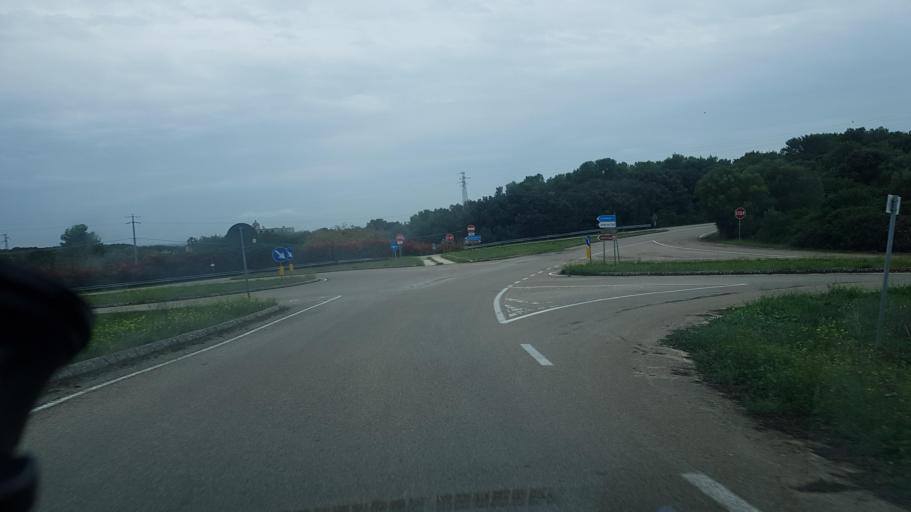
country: IT
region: Apulia
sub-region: Provincia di Brindisi
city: Ostuni
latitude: 40.7360
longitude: 17.5416
